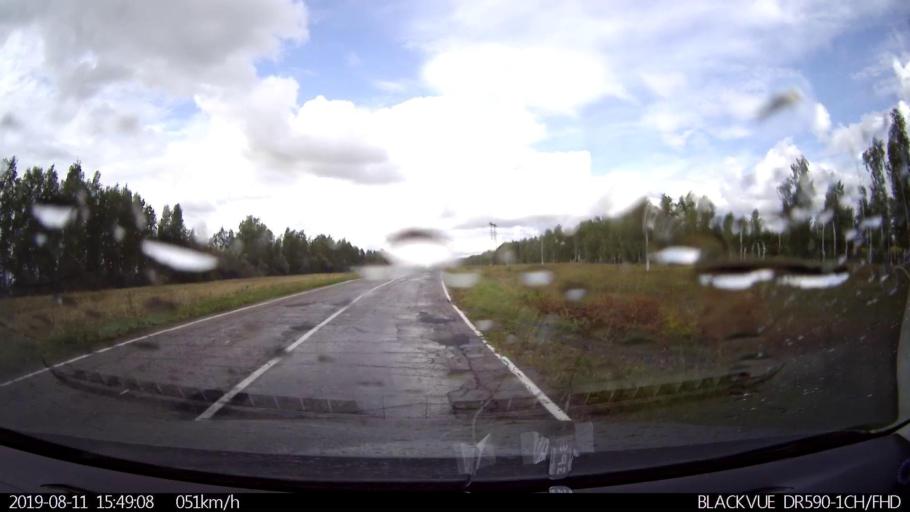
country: RU
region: Ulyanovsk
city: Ignatovka
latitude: 53.9021
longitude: 47.6547
